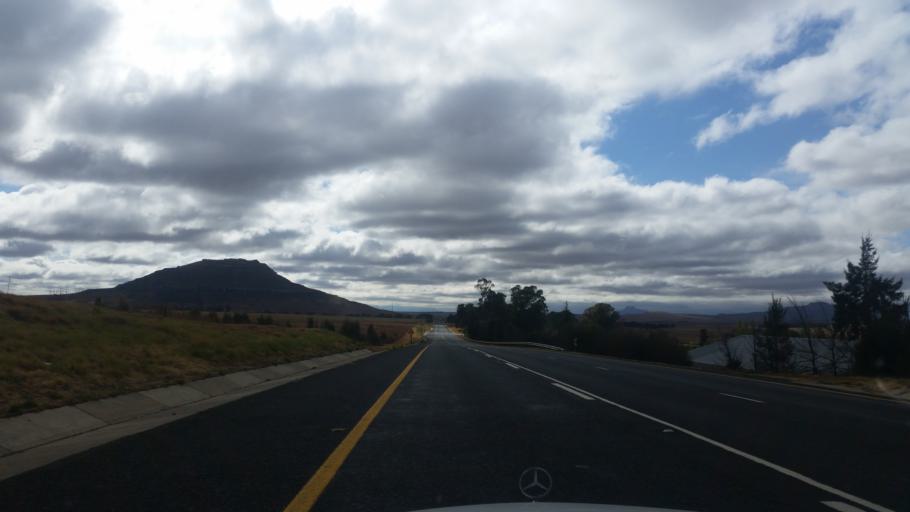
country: ZA
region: Orange Free State
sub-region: Thabo Mofutsanyana District Municipality
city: Phuthaditjhaba
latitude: -28.3133
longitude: 28.7241
